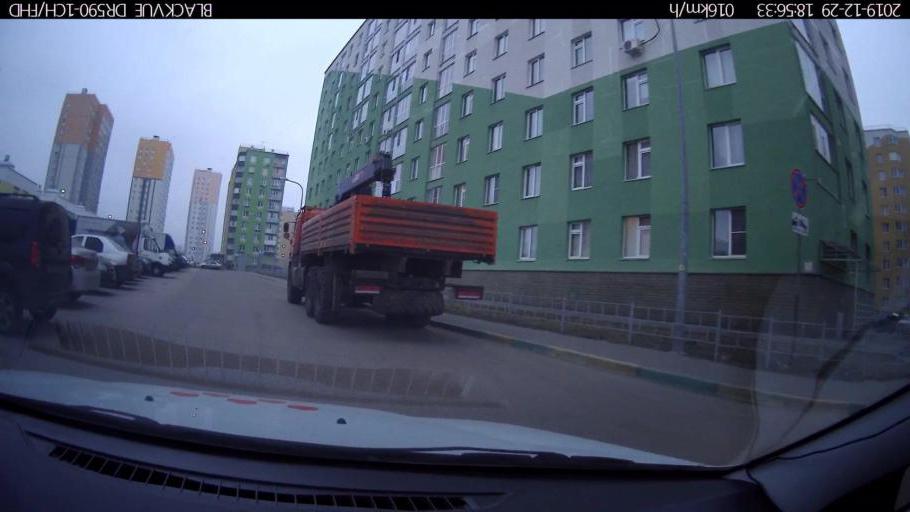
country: RU
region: Nizjnij Novgorod
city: Nizhniy Novgorod
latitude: 56.3419
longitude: 43.9141
